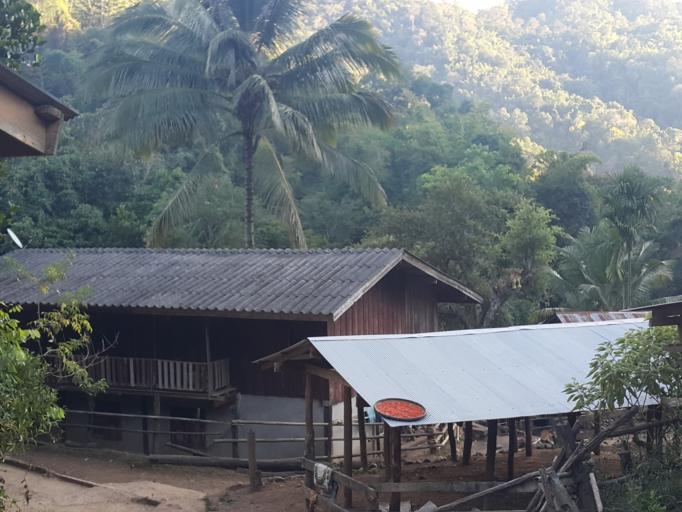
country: TH
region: Chiang Mai
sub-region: Amphoe Chiang Dao
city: Chiang Dao
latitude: 19.4365
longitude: 98.7937
